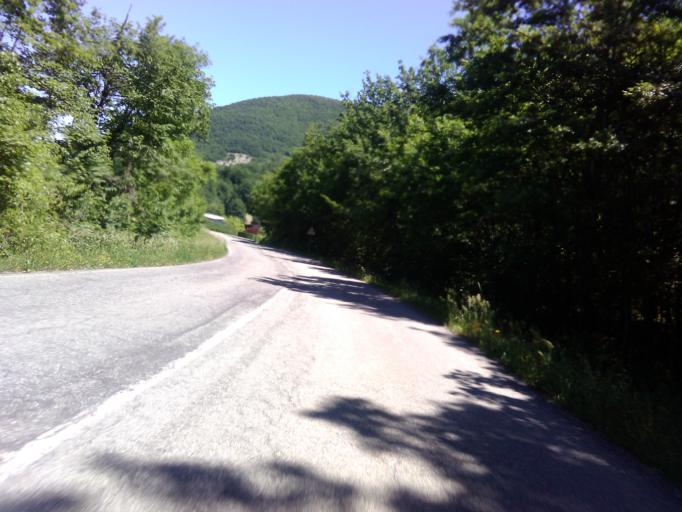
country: IT
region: Emilia-Romagna
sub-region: Provincia di Parma
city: Terenzo
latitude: 44.5615
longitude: 10.0465
